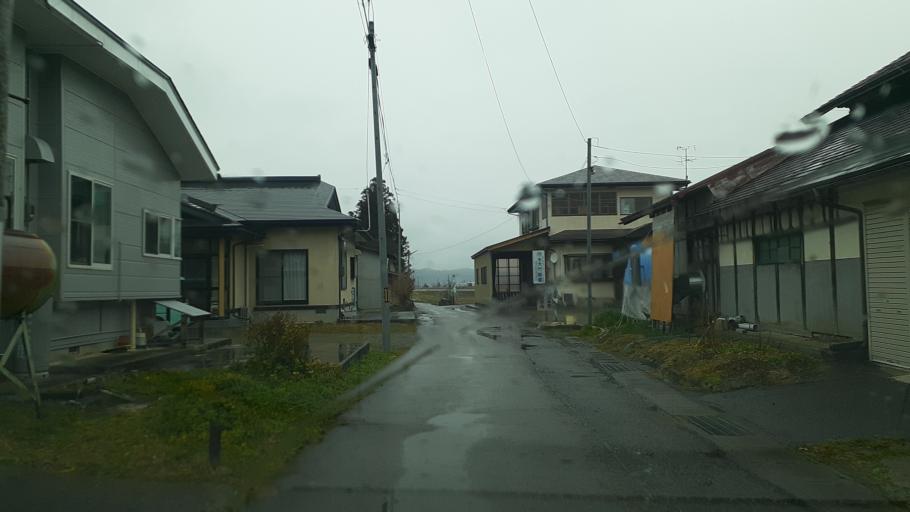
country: JP
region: Fukushima
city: Kitakata
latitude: 37.5850
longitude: 139.8440
